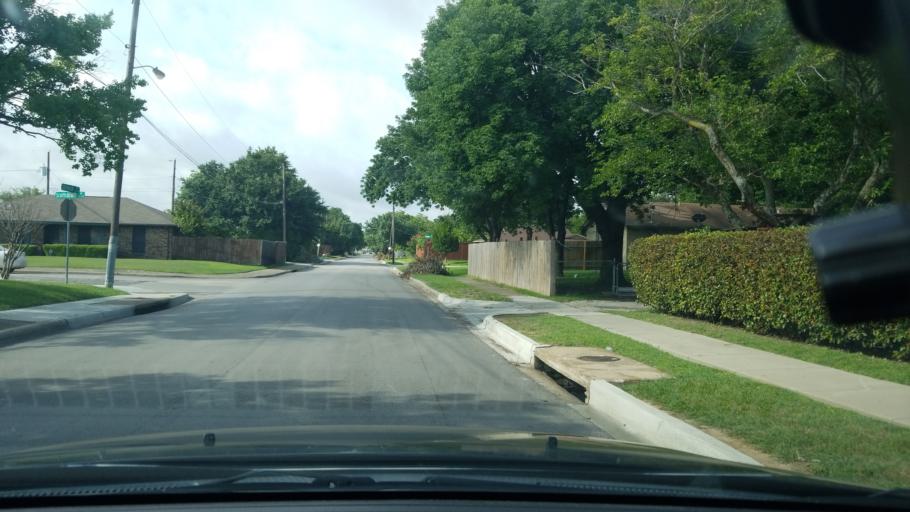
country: US
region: Texas
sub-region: Dallas County
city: Mesquite
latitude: 32.8175
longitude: -96.6685
